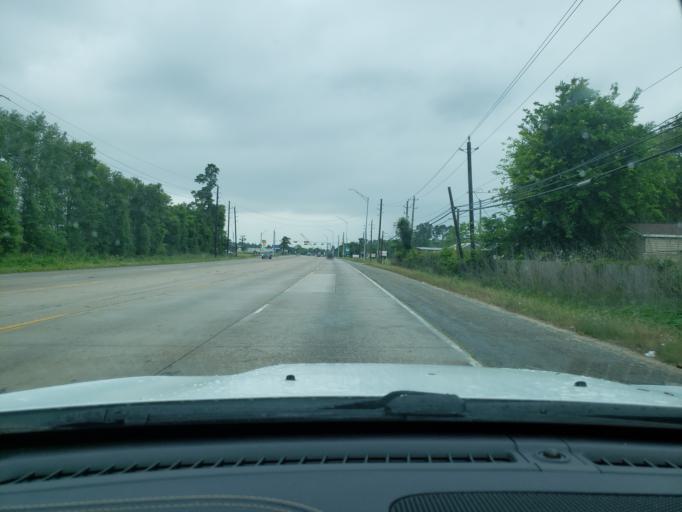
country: US
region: Texas
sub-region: Chambers County
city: Mont Belvieu
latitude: 29.7805
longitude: -94.9131
